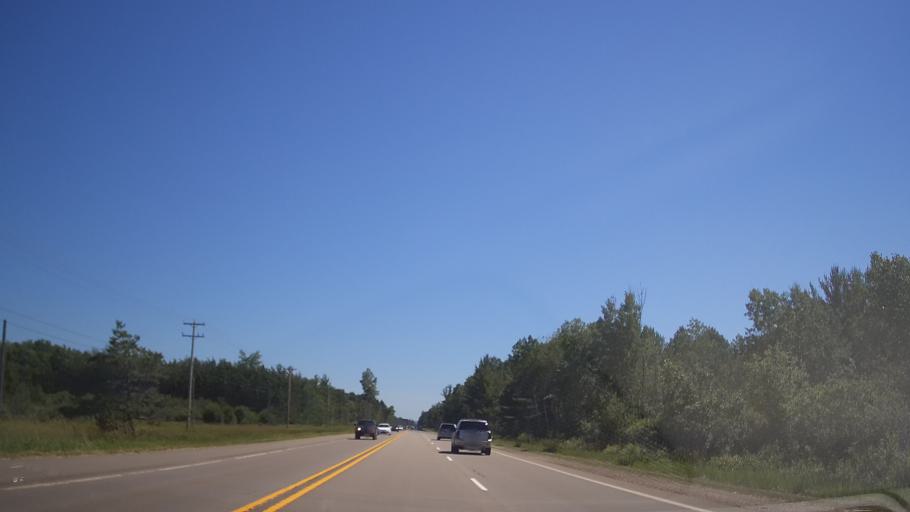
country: US
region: Michigan
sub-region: Cheboygan County
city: Indian River
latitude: 45.5284
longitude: -84.7818
